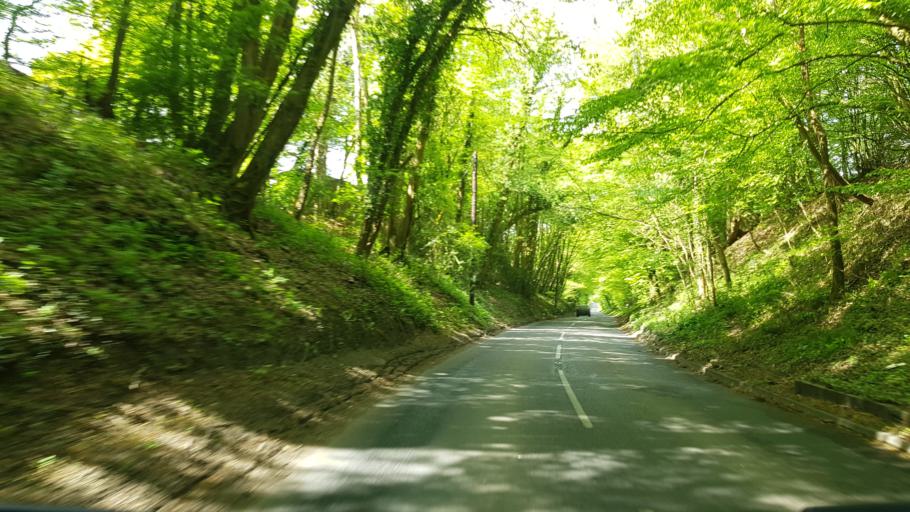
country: GB
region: England
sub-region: East Sussex
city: Robertsbridge
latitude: 51.0309
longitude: 0.4563
